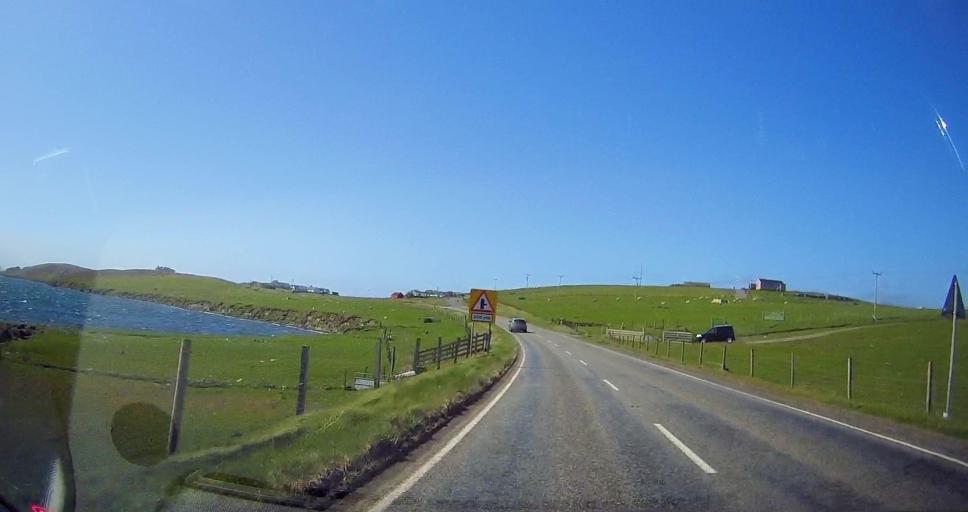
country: GB
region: Scotland
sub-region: Shetland Islands
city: Sandwick
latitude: 60.1265
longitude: -1.2799
